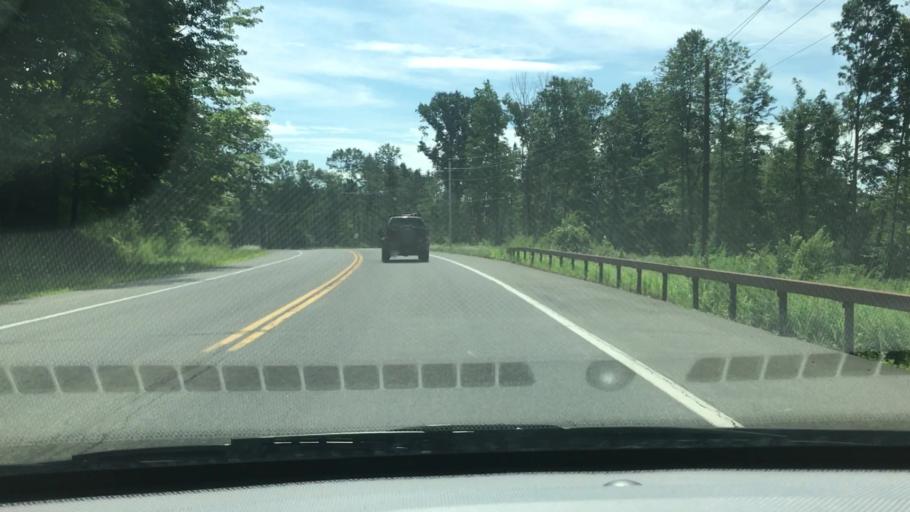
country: US
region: New York
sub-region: Ulster County
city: Shokan
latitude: 41.9735
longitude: -74.2396
